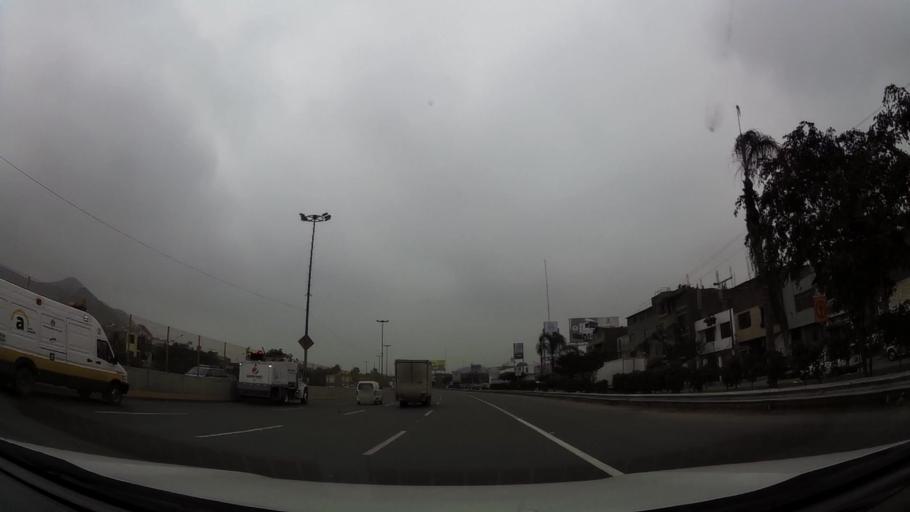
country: PE
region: Lima
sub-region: Lima
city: San Luis
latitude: -12.0529
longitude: -76.9756
